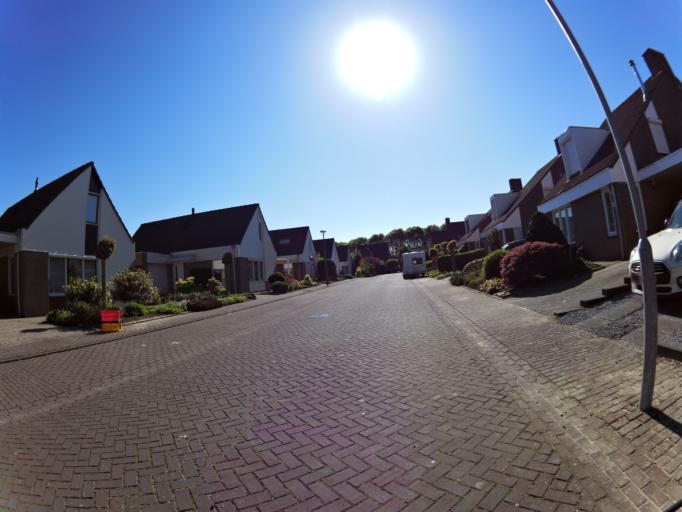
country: NL
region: Limburg
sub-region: Gemeente Schinnen
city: Oirsbeek
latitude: 50.9474
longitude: 5.9078
